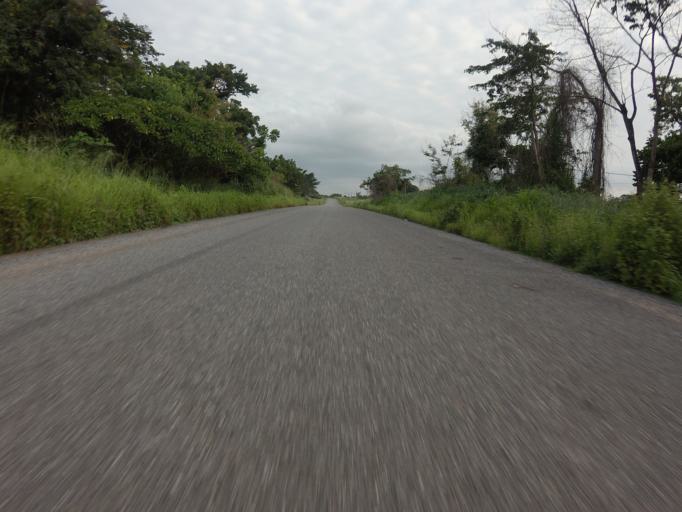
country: GH
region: Volta
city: Kpandu
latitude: 6.8599
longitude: 0.3962
